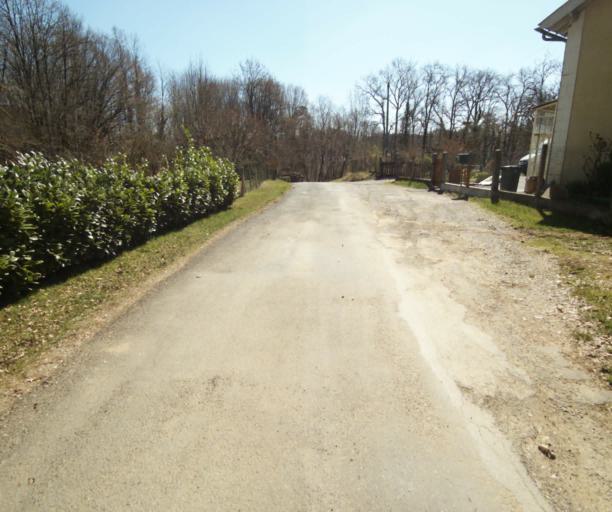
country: FR
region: Limousin
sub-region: Departement de la Correze
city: Saint-Clement
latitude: 45.3181
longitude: 1.7039
